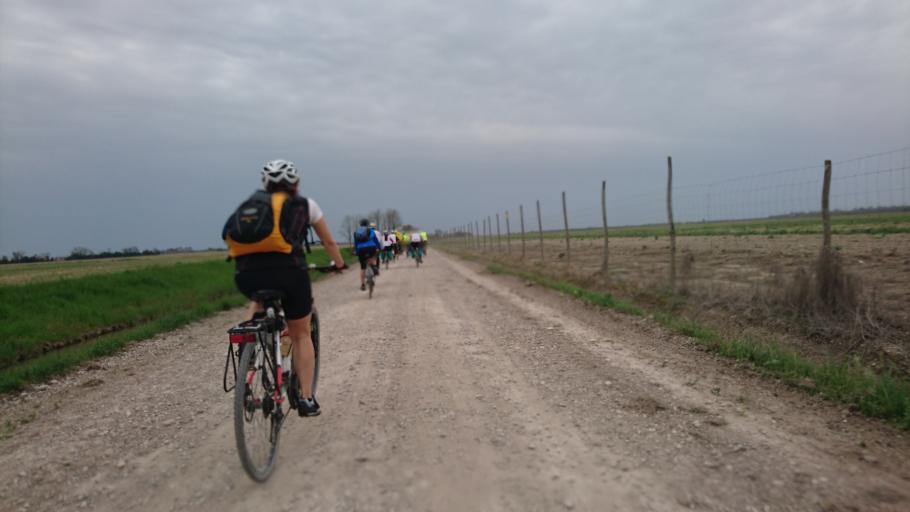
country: IT
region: Veneto
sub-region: Provincia di Venezia
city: Lugugnana
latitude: 45.6982
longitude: 12.9304
